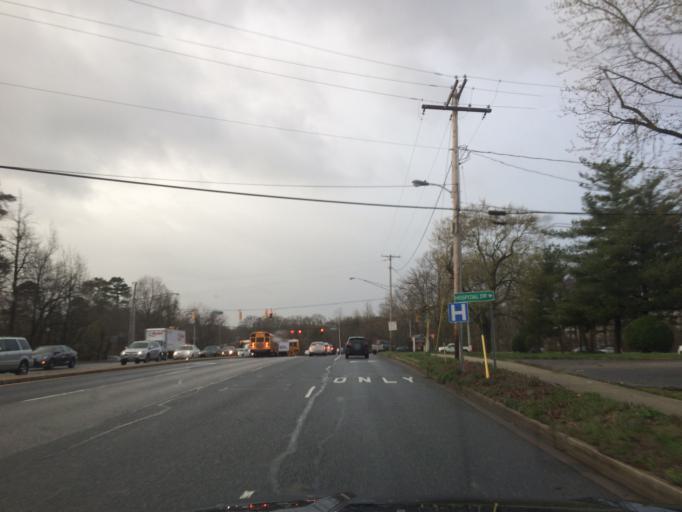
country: US
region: Maryland
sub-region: Anne Arundel County
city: South Gate
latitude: 39.1390
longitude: -76.6189
